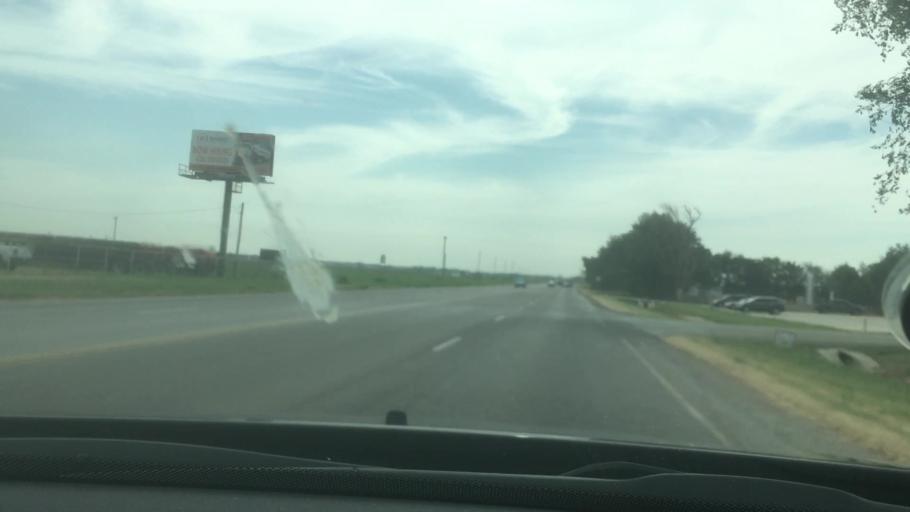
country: US
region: Oklahoma
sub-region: Garvin County
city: Lindsay
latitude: 34.8364
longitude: -97.5954
